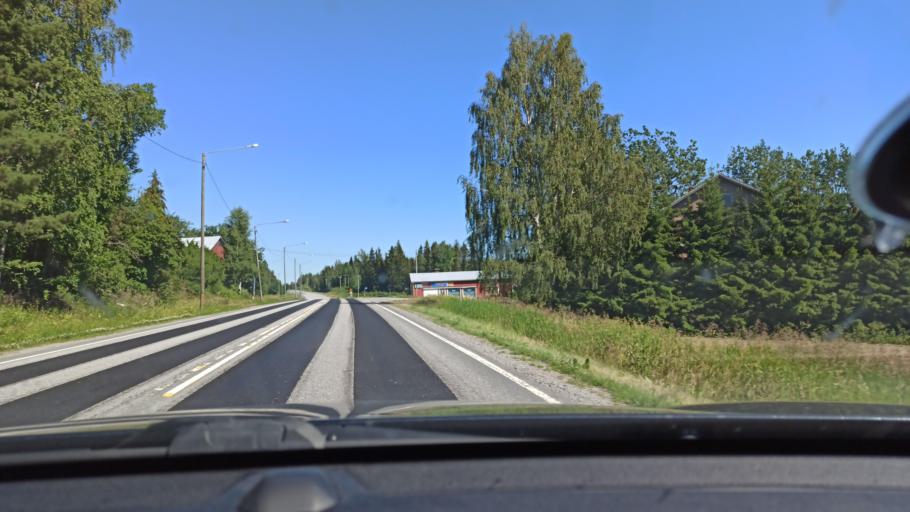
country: FI
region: Ostrobothnia
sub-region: Vaasa
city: Vaehaekyroe
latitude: 63.2025
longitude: 22.1120
